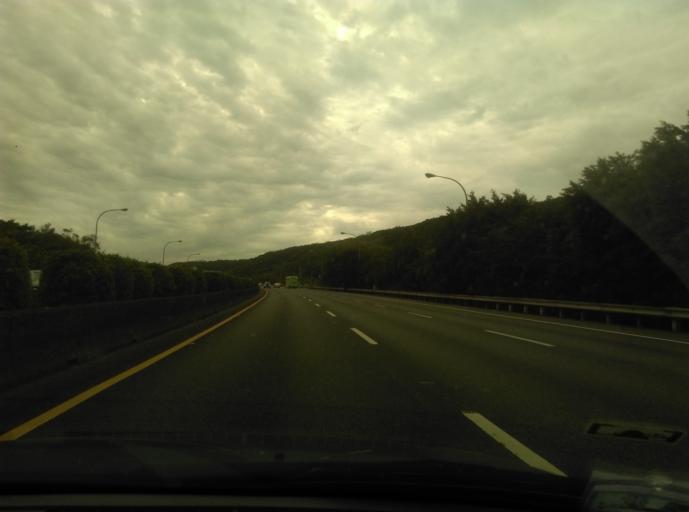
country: TW
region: Taiwan
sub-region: Taoyuan
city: Taoyuan
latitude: 24.9387
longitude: 121.3227
